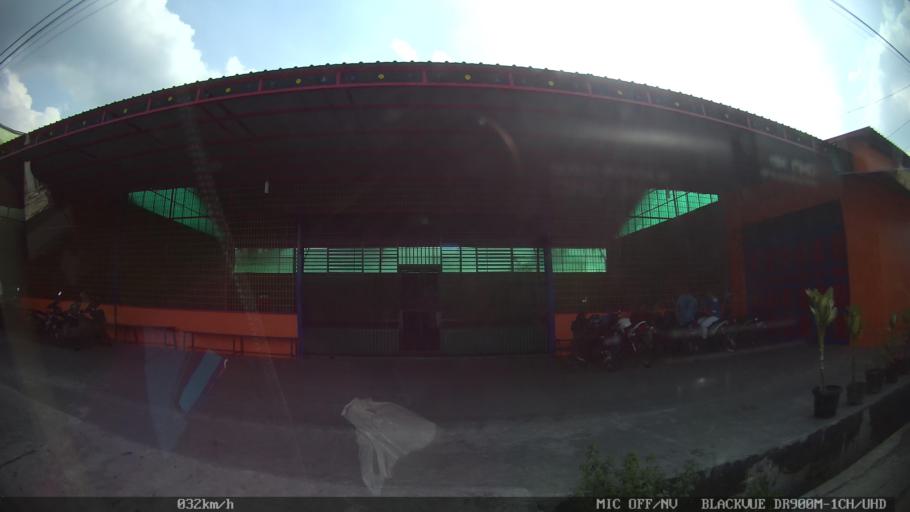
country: ID
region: North Sumatra
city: Binjai
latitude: 3.6148
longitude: 98.4980
